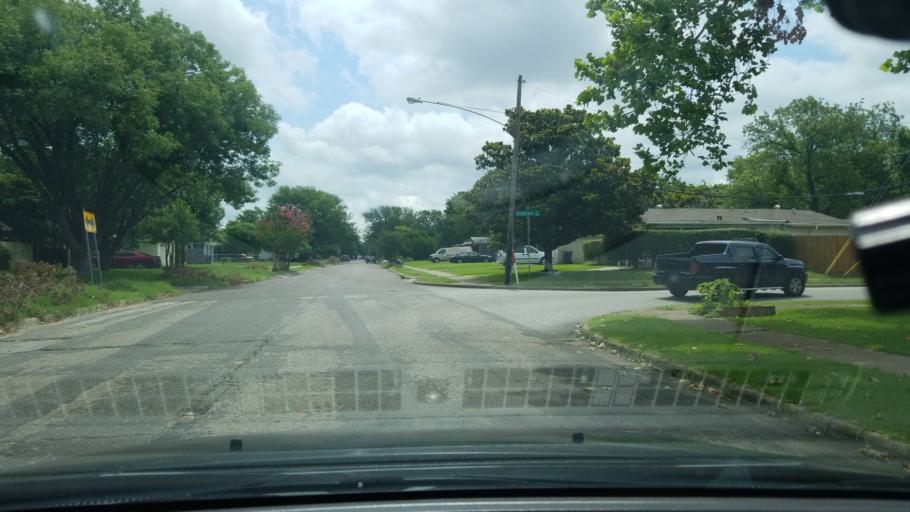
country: US
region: Texas
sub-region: Dallas County
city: Mesquite
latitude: 32.8206
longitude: -96.6735
